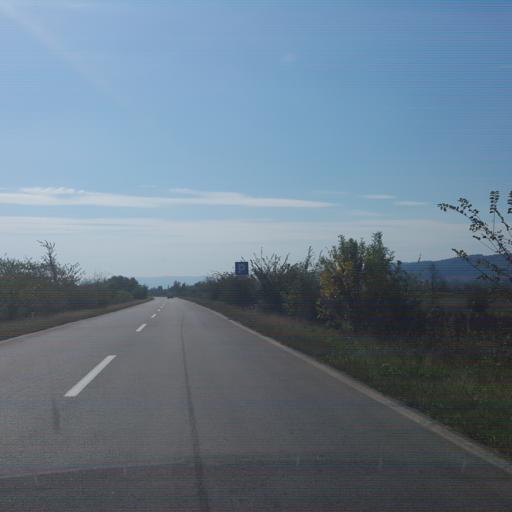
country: RS
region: Central Serbia
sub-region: Zajecarski Okrug
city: Knjazevac
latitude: 43.6556
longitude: 22.2831
